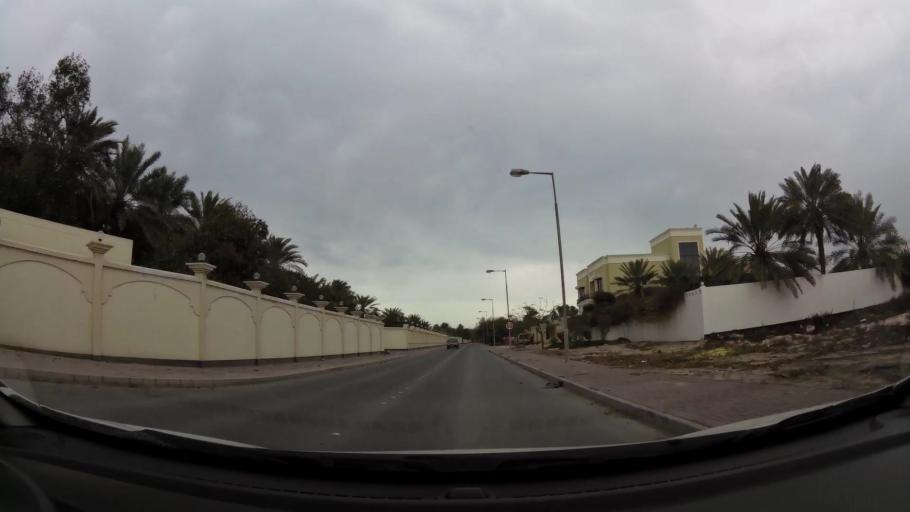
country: BH
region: Central Governorate
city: Madinat Hamad
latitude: 26.1492
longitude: 50.4551
